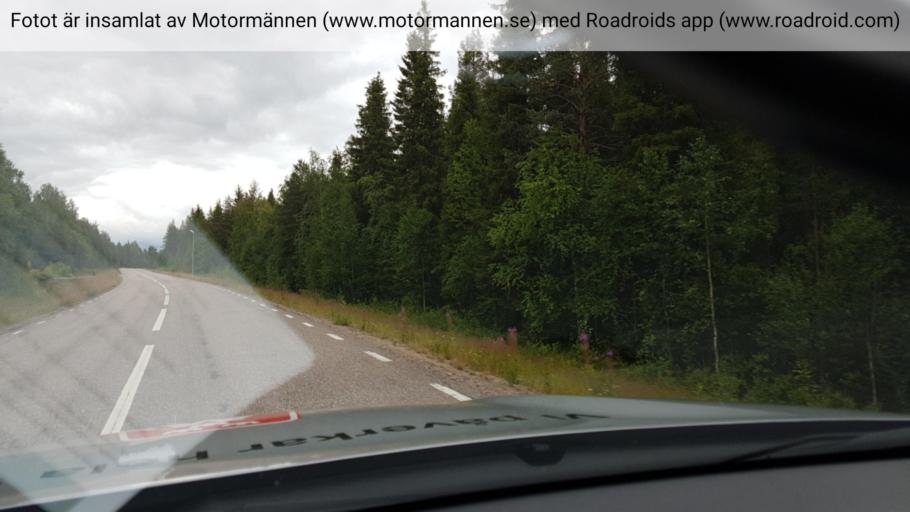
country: SE
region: Norrbotten
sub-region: Overkalix Kommun
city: OEverkalix
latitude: 66.7321
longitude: 22.8872
